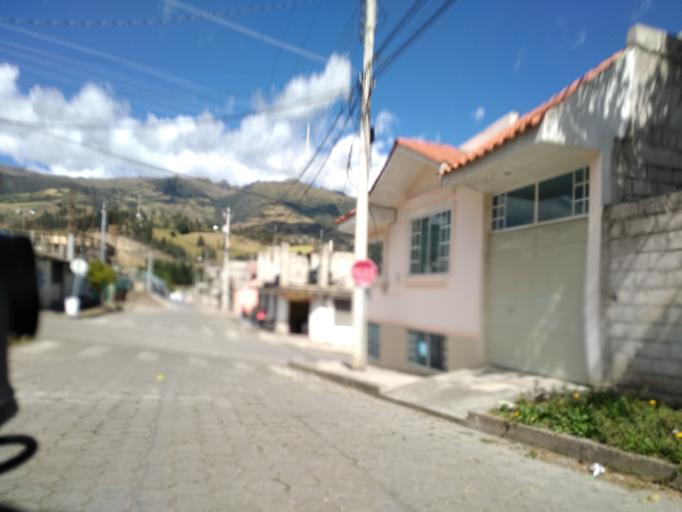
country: EC
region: Imbabura
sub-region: Canton Otavalo
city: Otavalo
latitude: 0.1798
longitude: -78.2026
